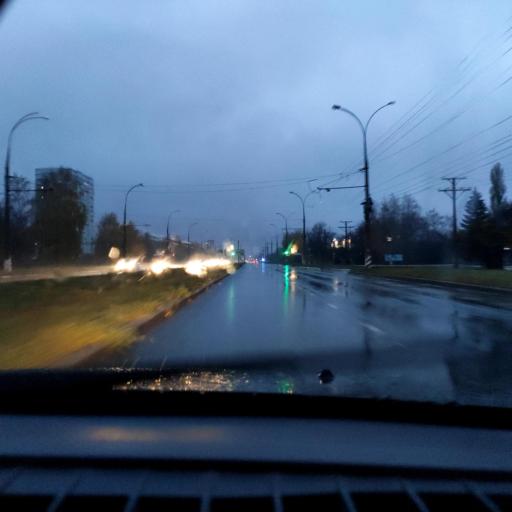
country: RU
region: Samara
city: Tol'yatti
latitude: 53.5446
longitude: 49.3011
